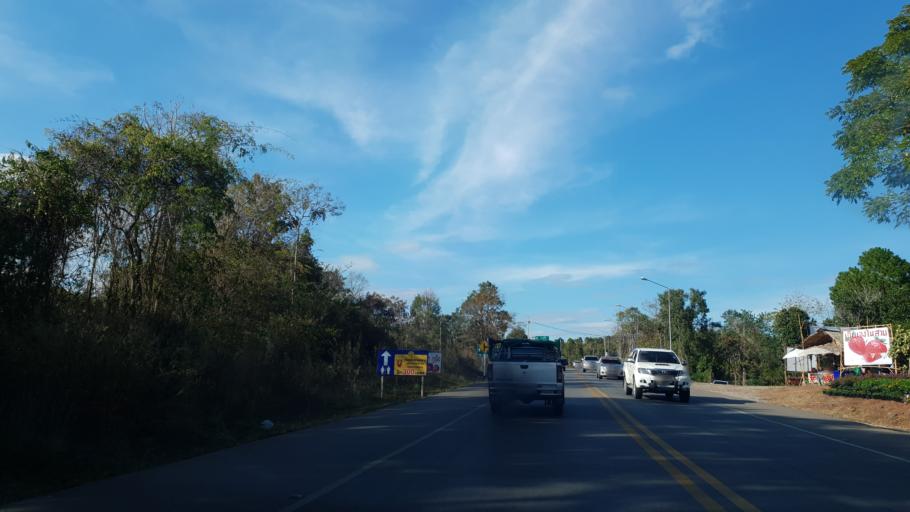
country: TH
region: Loei
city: Phu Ruea
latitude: 17.4435
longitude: 101.4675
